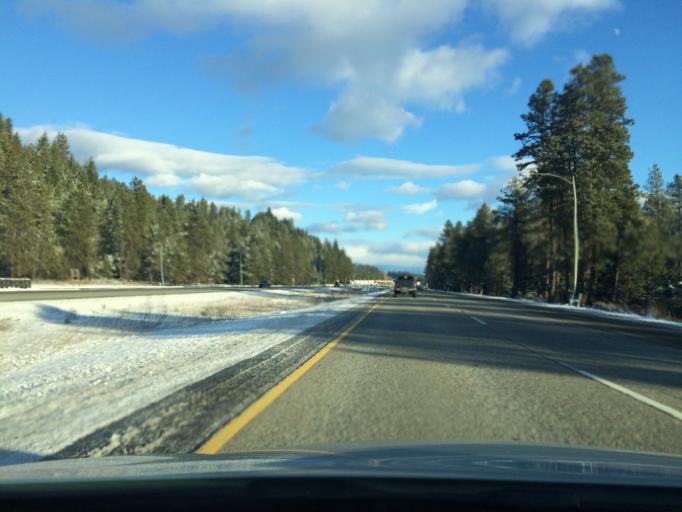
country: US
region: Washington
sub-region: Kittitas County
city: Cle Elum
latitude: 47.1827
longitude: -121.0273
